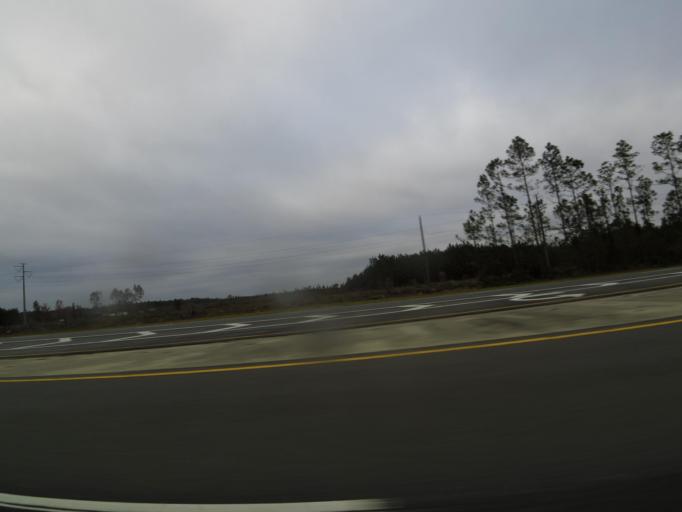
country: US
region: Georgia
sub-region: Charlton County
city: Folkston
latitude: 30.8844
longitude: -82.0405
